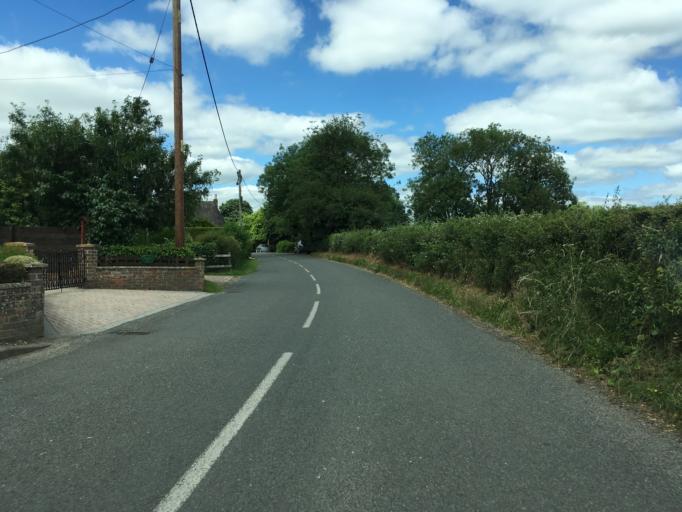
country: GB
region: England
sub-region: Hampshire
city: Highclere
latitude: 51.2552
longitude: -1.4069
